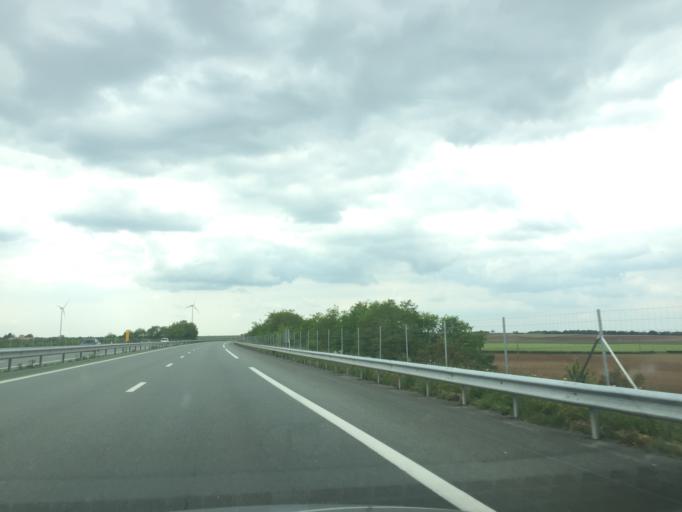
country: FR
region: Pays de la Loire
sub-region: Departement de la Vendee
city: Benet
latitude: 46.4040
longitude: -0.5918
